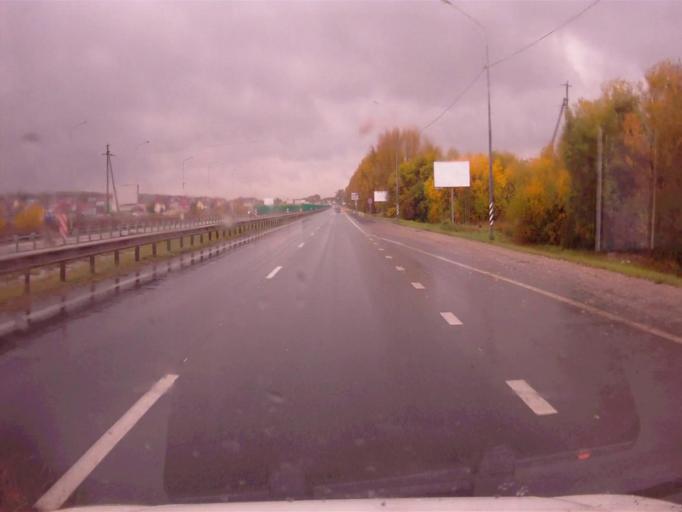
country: RU
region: Chelyabinsk
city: Dolgoderevenskoye
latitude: 55.2773
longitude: 61.3437
